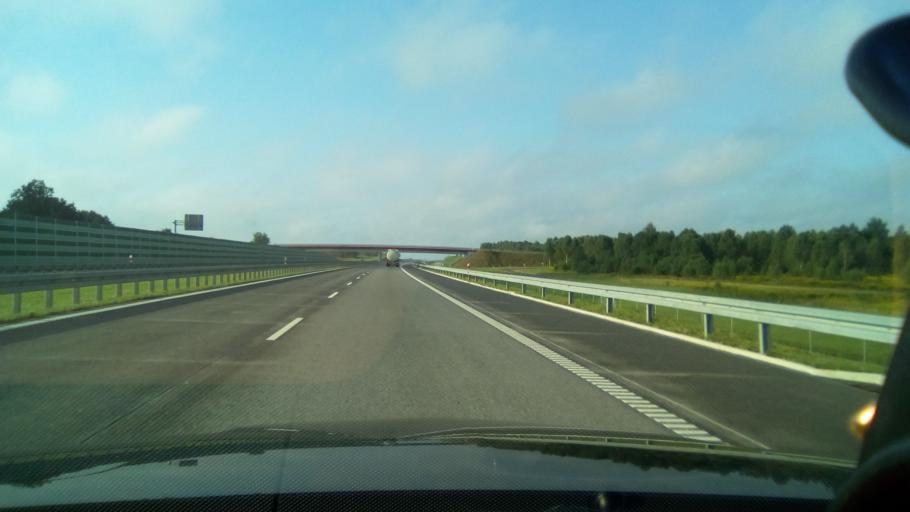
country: PL
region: Silesian Voivodeship
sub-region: Powiat czestochowski
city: Starcza
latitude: 50.6819
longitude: 19.0540
